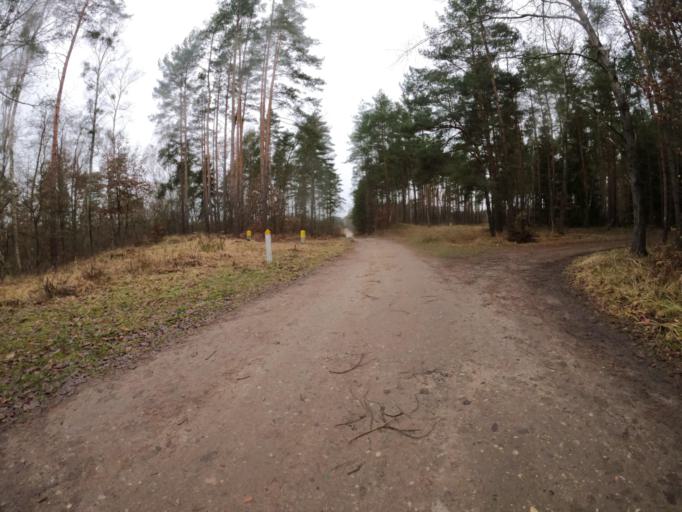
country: PL
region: West Pomeranian Voivodeship
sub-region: Powiat mysliborski
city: Debno
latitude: 52.7567
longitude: 14.7672
